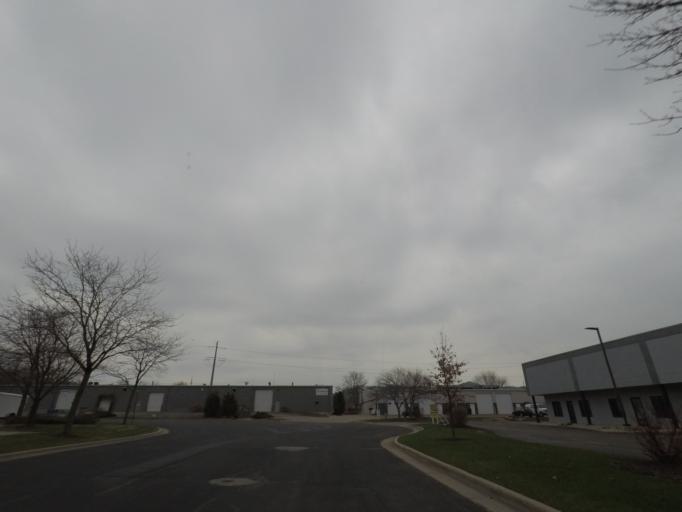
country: US
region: Wisconsin
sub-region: Dane County
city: Middleton
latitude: 43.0974
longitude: -89.5421
